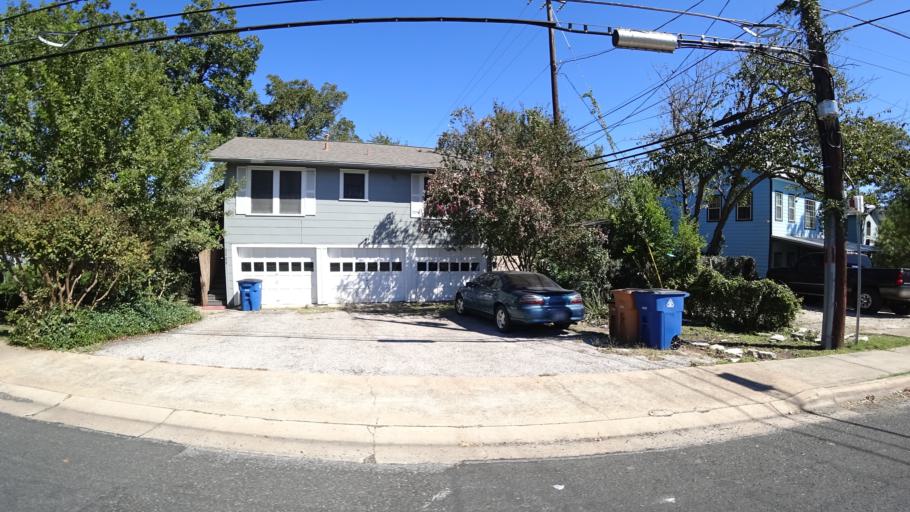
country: US
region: Texas
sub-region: Travis County
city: Austin
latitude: 30.2369
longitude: -97.7440
